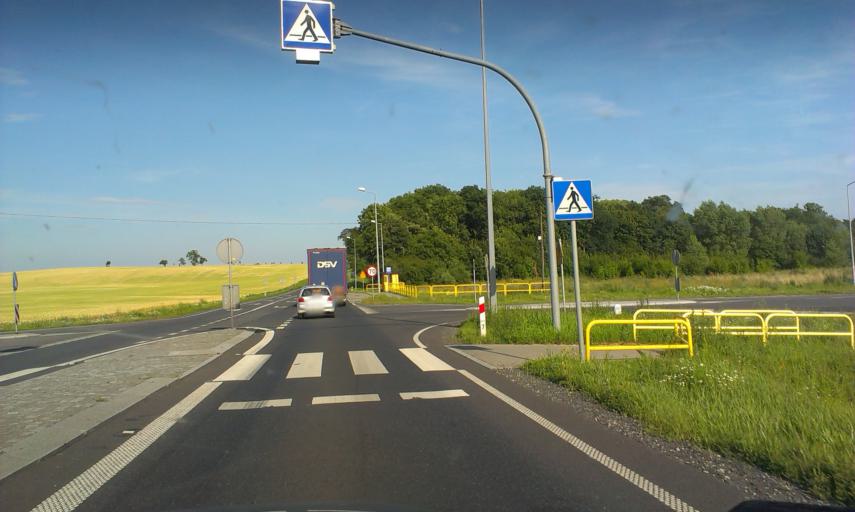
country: PL
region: Kujawsko-Pomorskie
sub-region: Powiat nakielski
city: Naklo nad Notecia
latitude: 53.1470
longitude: 17.5286
